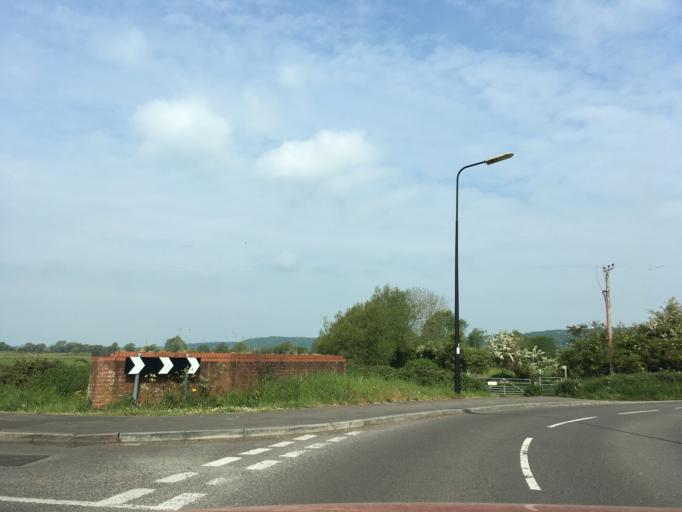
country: GB
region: England
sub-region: North Somerset
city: Nailsea
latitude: 51.4314
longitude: -2.7806
